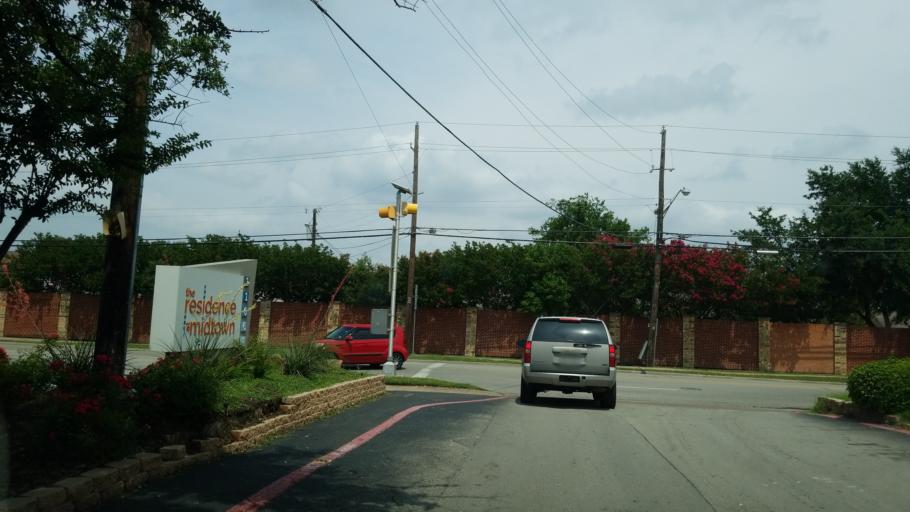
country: US
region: Texas
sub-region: Dallas County
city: Farmers Branch
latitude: 32.9074
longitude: -96.8811
